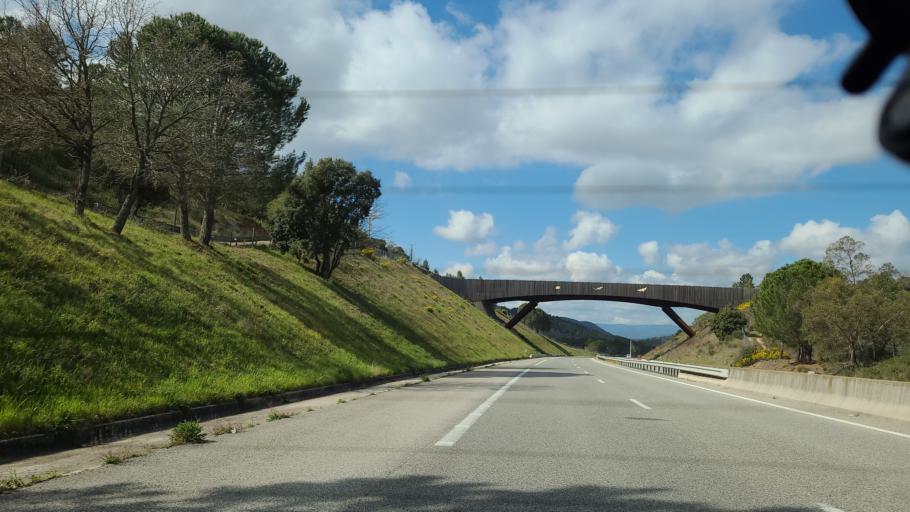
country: FR
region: Provence-Alpes-Cote d'Azur
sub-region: Departement du Var
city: Pignans
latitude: 43.2902
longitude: 6.2518
